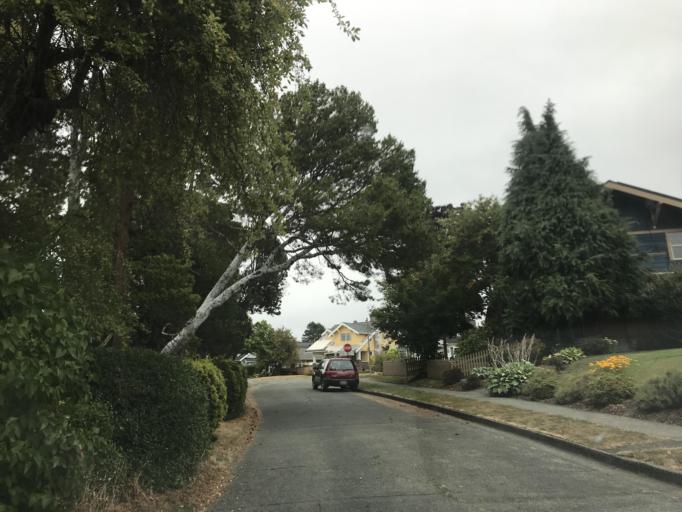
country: US
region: Washington
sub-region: Whatcom County
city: Bellingham
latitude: 48.7649
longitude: -122.4762
